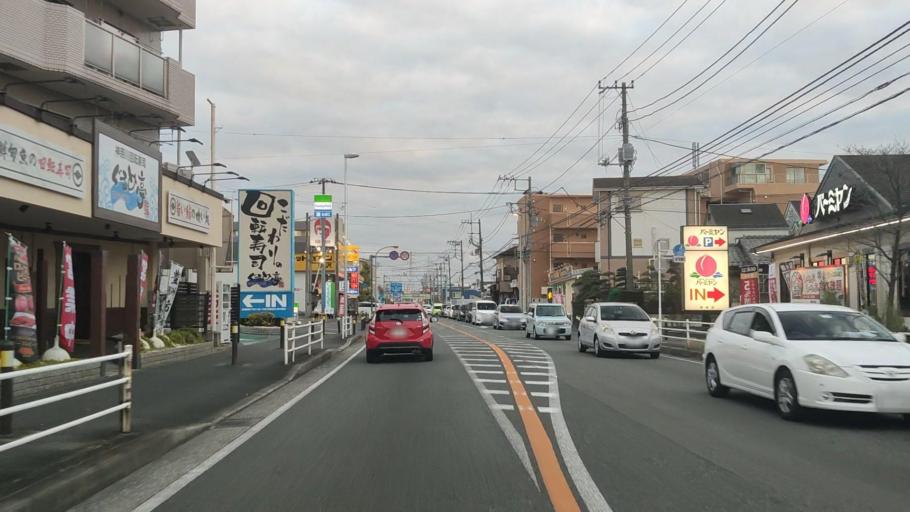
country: JP
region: Kanagawa
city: Minami-rinkan
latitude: 35.4193
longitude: 139.4691
